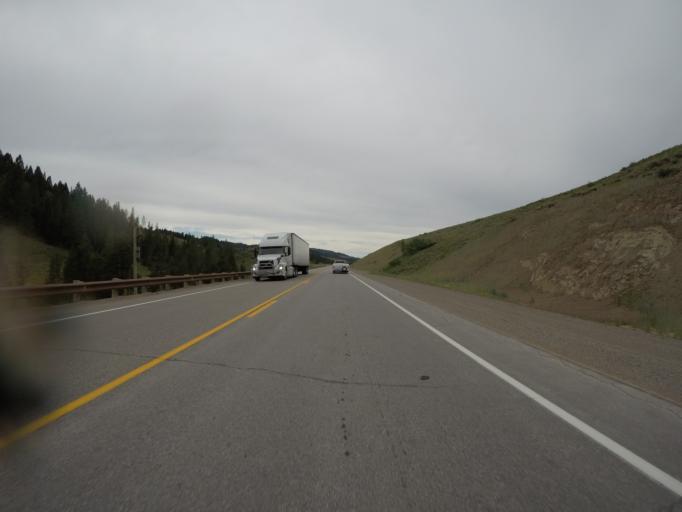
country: US
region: Wyoming
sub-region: Lincoln County
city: Afton
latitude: 42.5246
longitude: -110.8962
